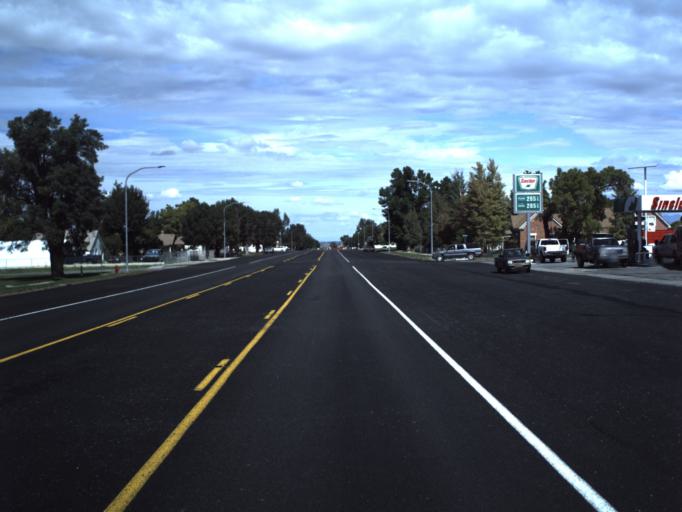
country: US
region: Utah
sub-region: Millard County
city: Fillmore
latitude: 38.7983
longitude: -112.4377
